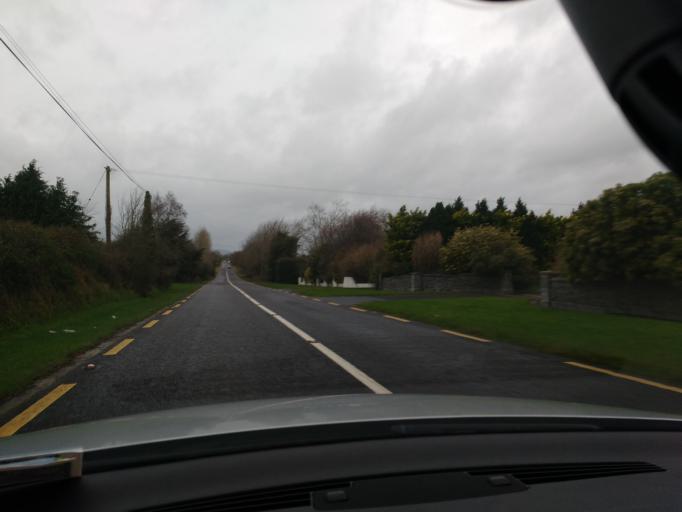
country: IE
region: Munster
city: Thurles
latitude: 52.6716
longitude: -7.7322
